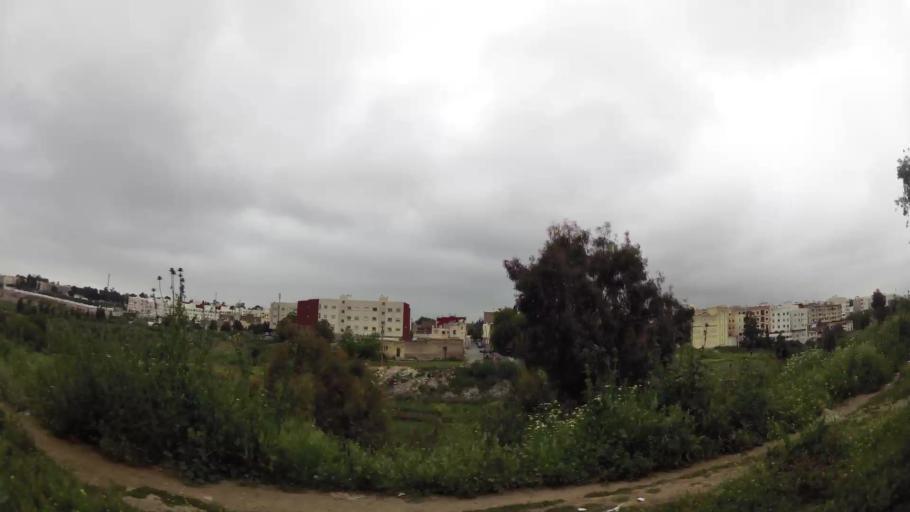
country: MA
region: Fes-Boulemane
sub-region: Fes
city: Fes
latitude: 34.0354
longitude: -4.9930
